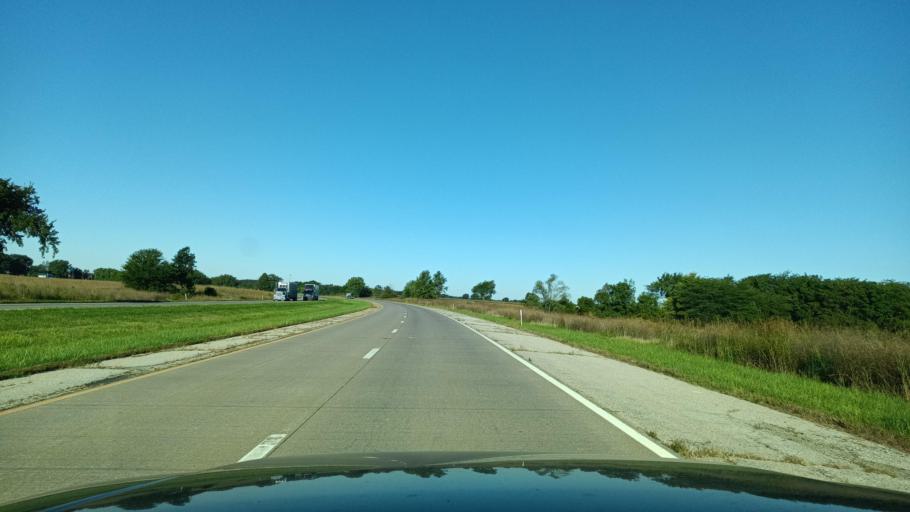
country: US
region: Illinois
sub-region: Warren County
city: Monmouth
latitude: 40.9267
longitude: -90.5825
